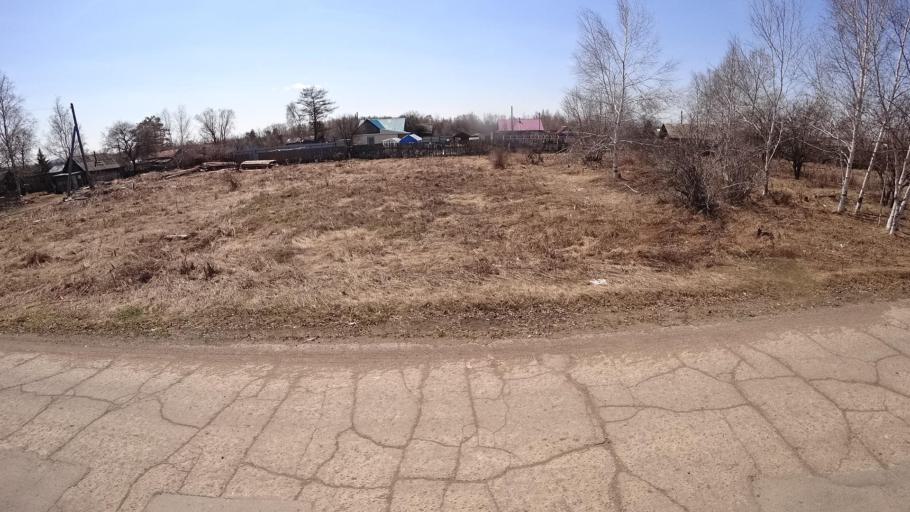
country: RU
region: Khabarovsk Krai
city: Khurba
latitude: 50.4064
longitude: 136.8784
